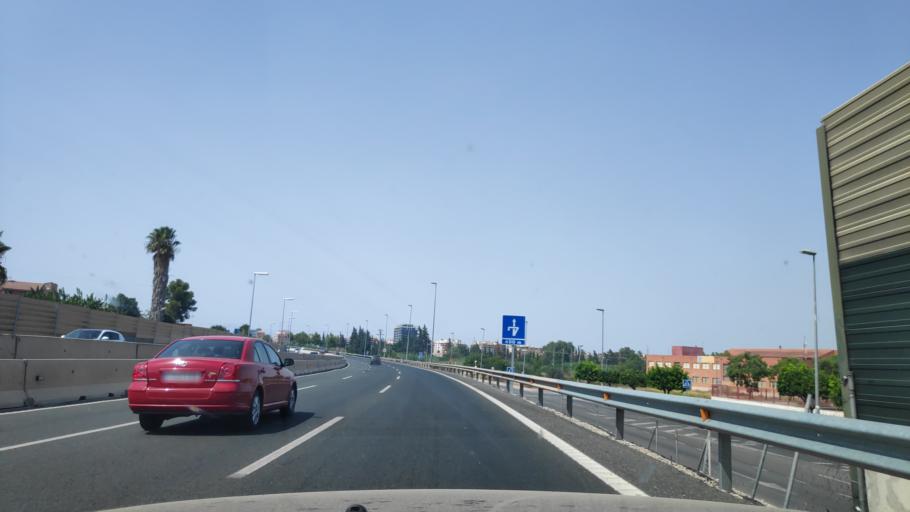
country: ES
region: Murcia
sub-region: Murcia
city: Murcia
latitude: 37.9601
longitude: -1.1351
